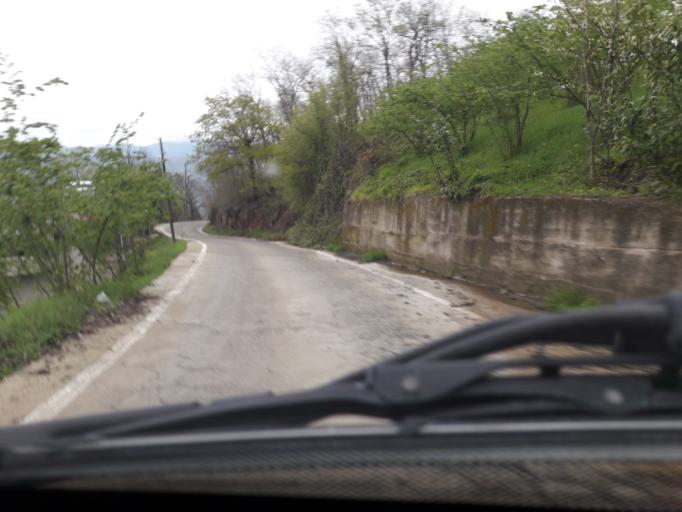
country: TR
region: Trabzon
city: Duzkoy
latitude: 40.9010
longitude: 39.4845
